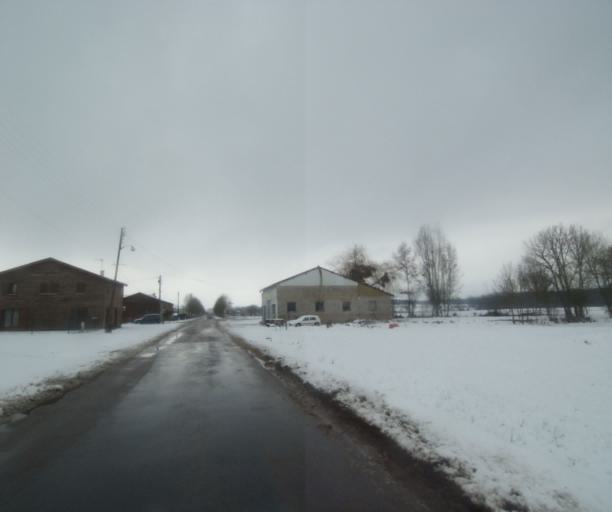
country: FR
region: Champagne-Ardenne
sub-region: Departement de la Haute-Marne
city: Montier-en-Der
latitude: 48.4735
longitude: 4.7859
